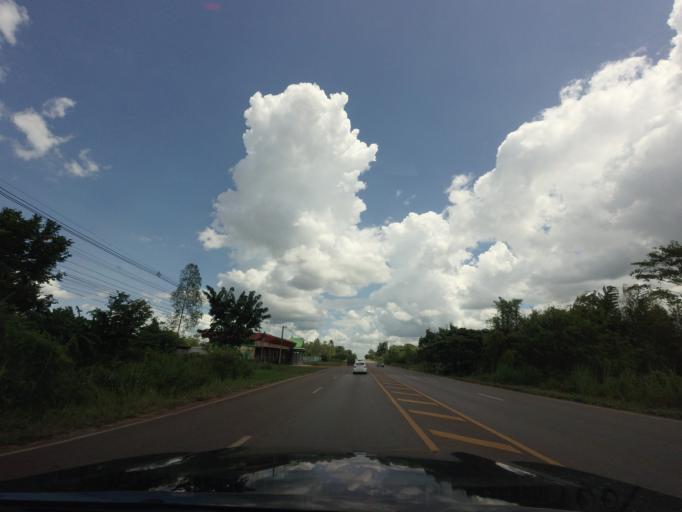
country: TH
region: Changwat Udon Thani
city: Ban Dung
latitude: 17.6851
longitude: 103.2079
